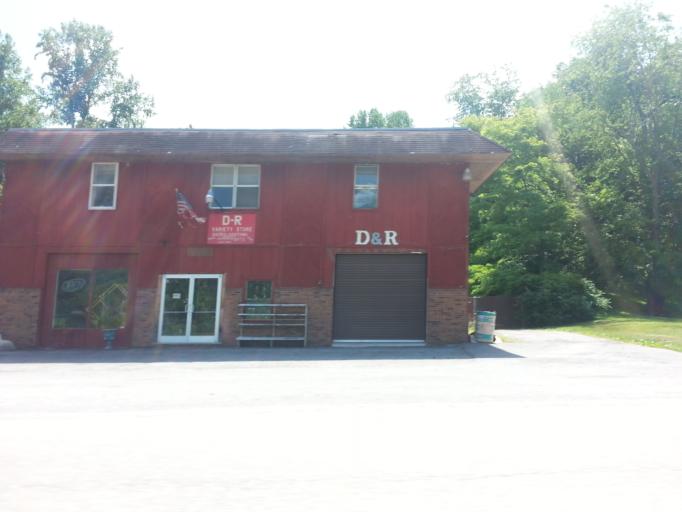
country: US
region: Virginia
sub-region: Lee County
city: Pennington Gap
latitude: 36.7679
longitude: -83.0315
